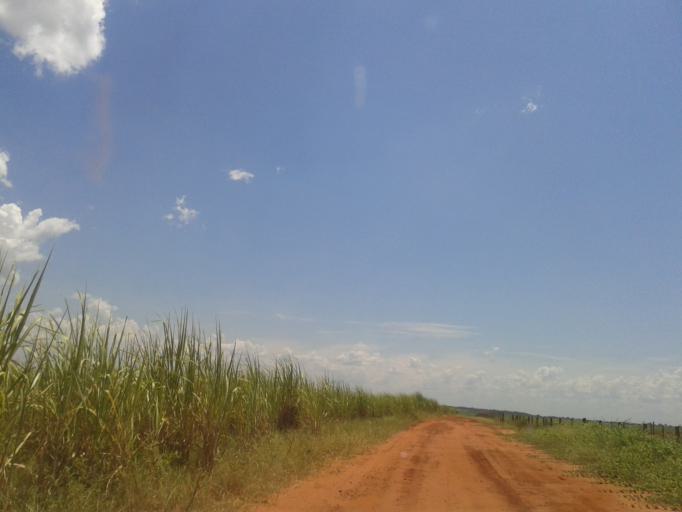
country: BR
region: Minas Gerais
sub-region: Santa Vitoria
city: Santa Vitoria
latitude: -19.1653
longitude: -50.4208
